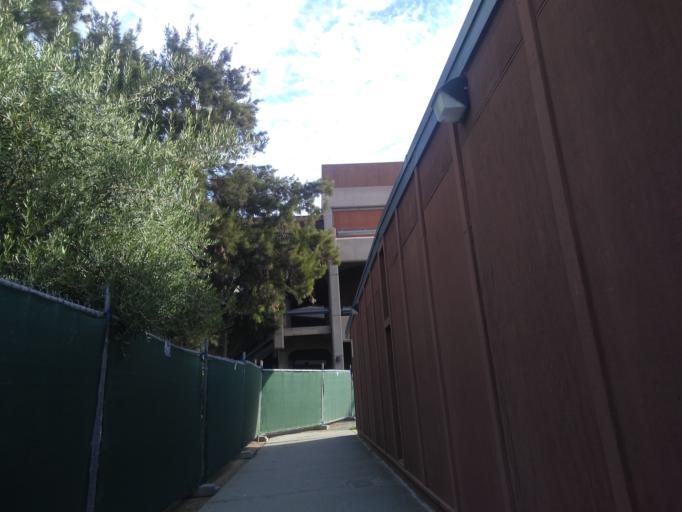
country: US
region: California
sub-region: Santa Clara County
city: Santa Clara
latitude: 37.3907
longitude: -121.9830
